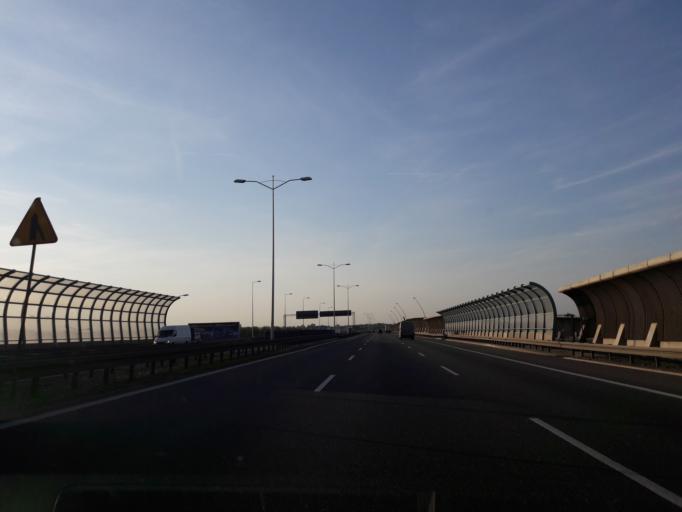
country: PL
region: Lower Silesian Voivodeship
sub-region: Powiat wroclawski
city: Smolec
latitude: 51.0663
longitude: 16.9291
